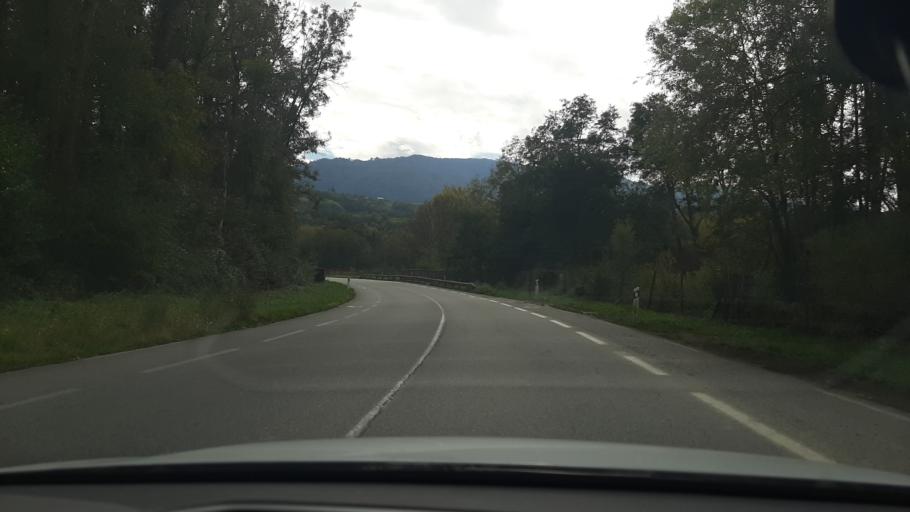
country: FR
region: Rhone-Alpes
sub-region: Departement de la Savoie
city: Montmelian
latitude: 45.4636
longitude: 6.0462
